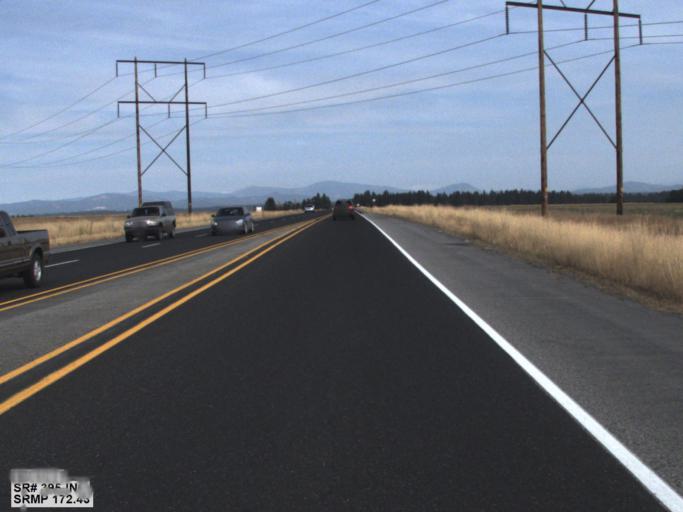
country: US
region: Washington
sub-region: Spokane County
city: Fairwood
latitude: 47.8505
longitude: -117.4218
